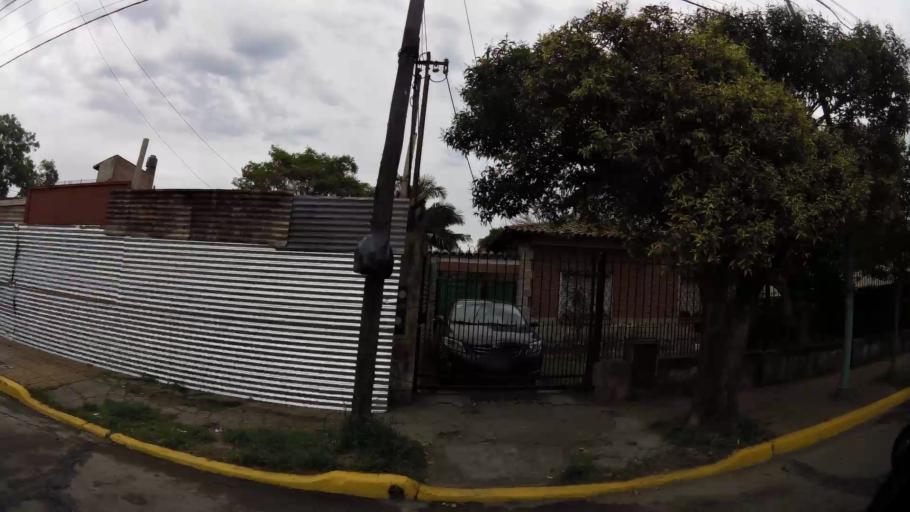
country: AR
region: Buenos Aires
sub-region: Partido de Quilmes
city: Quilmes
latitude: -34.7617
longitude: -58.2038
